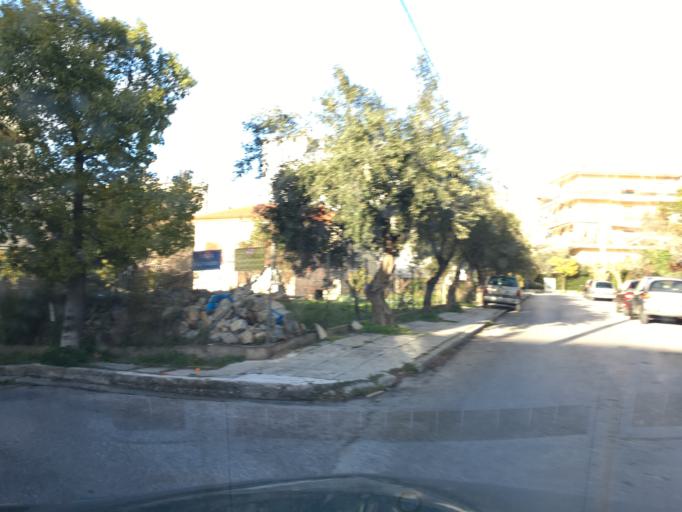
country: GR
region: Attica
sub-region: Nomarchia Athinas
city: Khalandrion
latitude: 38.0280
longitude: 23.7990
